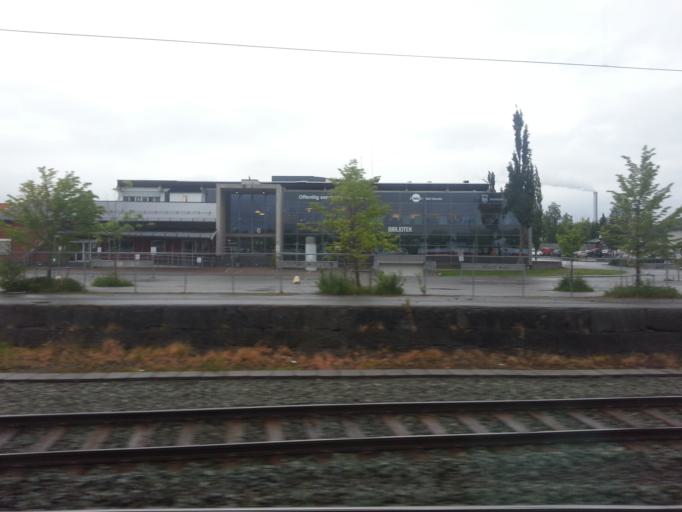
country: NO
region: Sor-Trondelag
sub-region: Trondheim
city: Trondheim
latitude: 63.3526
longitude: 10.3582
